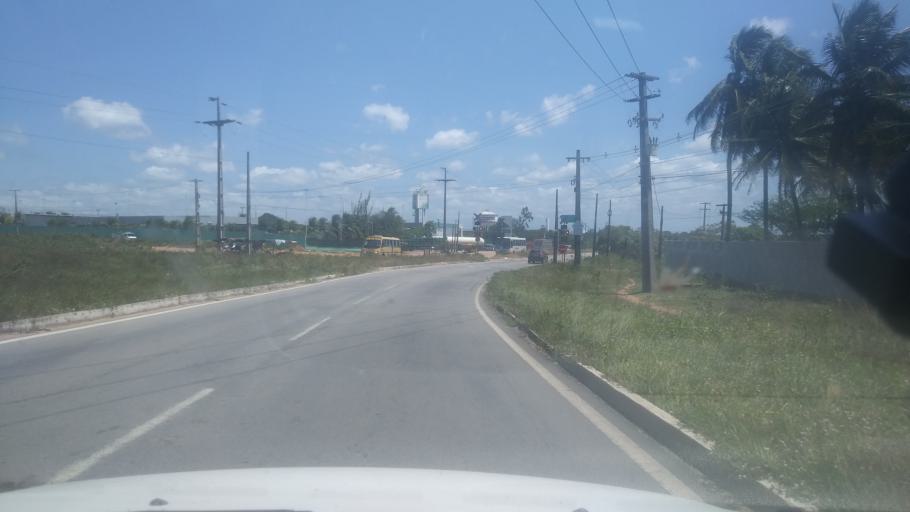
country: BR
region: Rio Grande do Norte
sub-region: Extremoz
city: Extremoz
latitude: -5.7231
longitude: -35.2790
